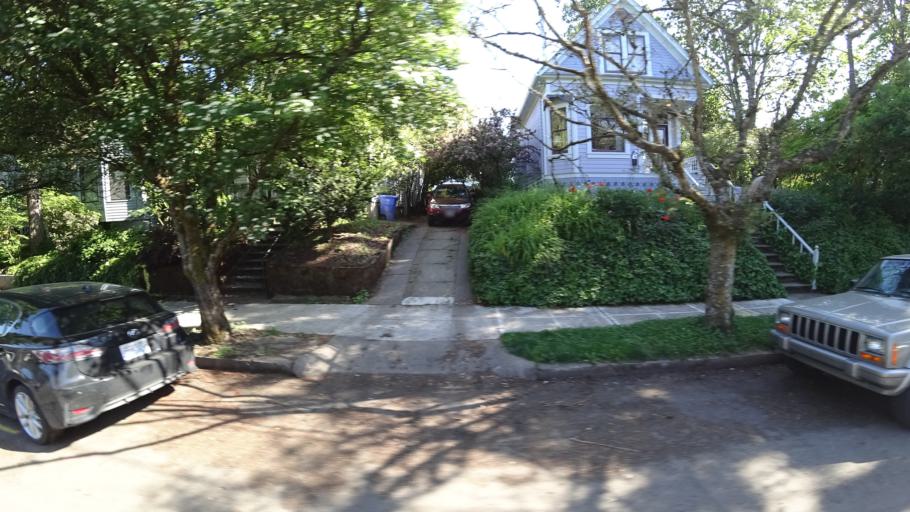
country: US
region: Oregon
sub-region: Multnomah County
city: Portland
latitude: 45.5390
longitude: -122.6627
